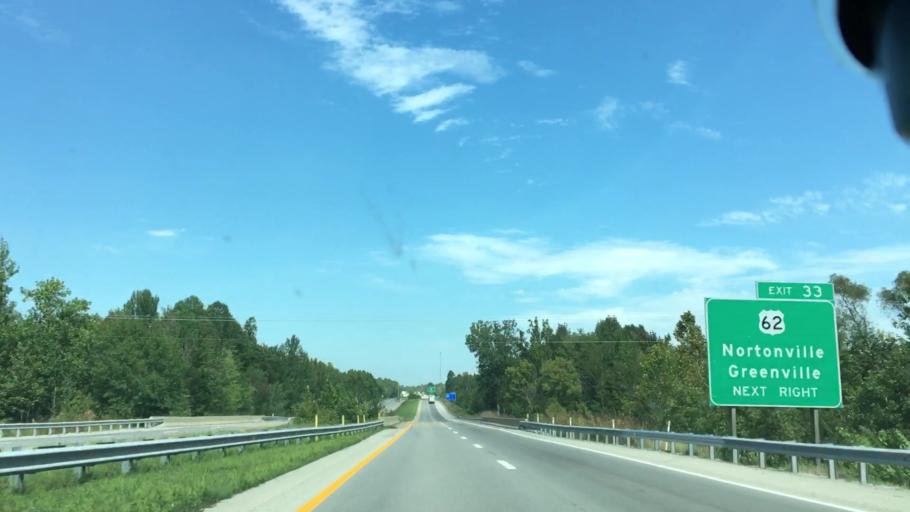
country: US
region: Kentucky
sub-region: Hopkins County
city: Nortonville
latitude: 37.1837
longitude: -87.4448
